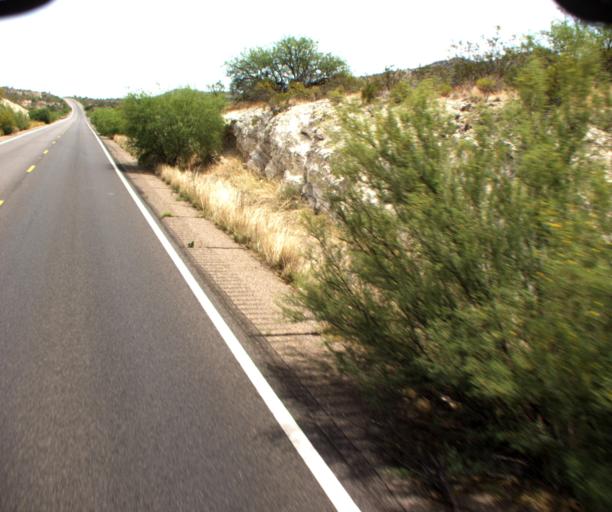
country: US
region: Arizona
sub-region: Gila County
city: Peridot
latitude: 33.2875
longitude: -110.3879
